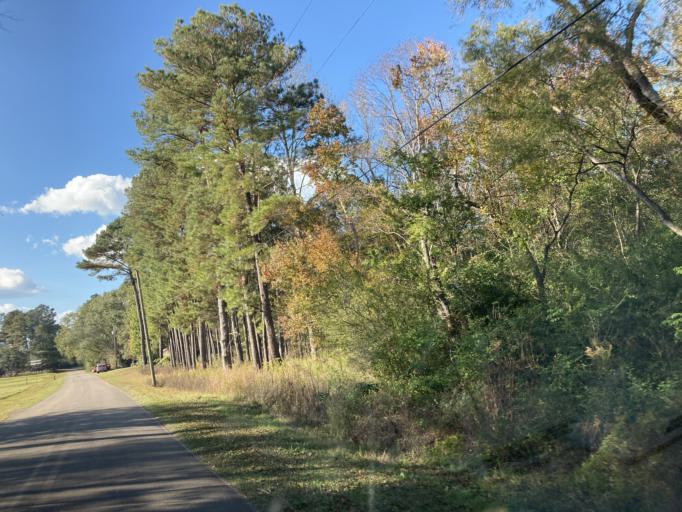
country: US
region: Mississippi
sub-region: Lamar County
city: Sumrall
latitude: 31.4291
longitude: -89.6515
